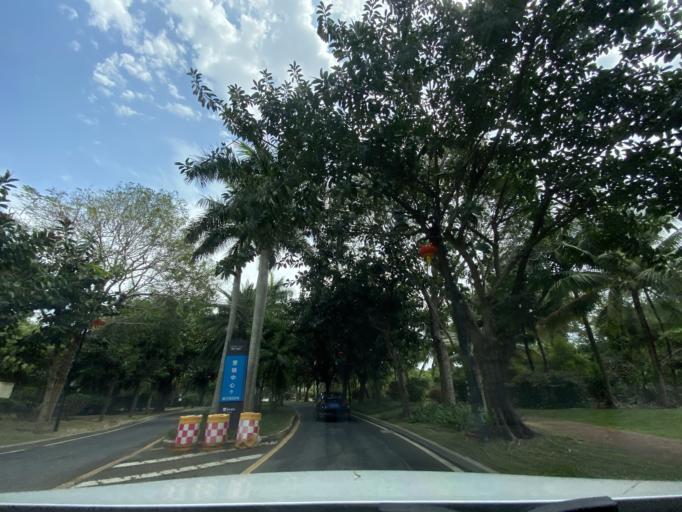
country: CN
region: Hainan
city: Liji
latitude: 18.6695
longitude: 110.2683
